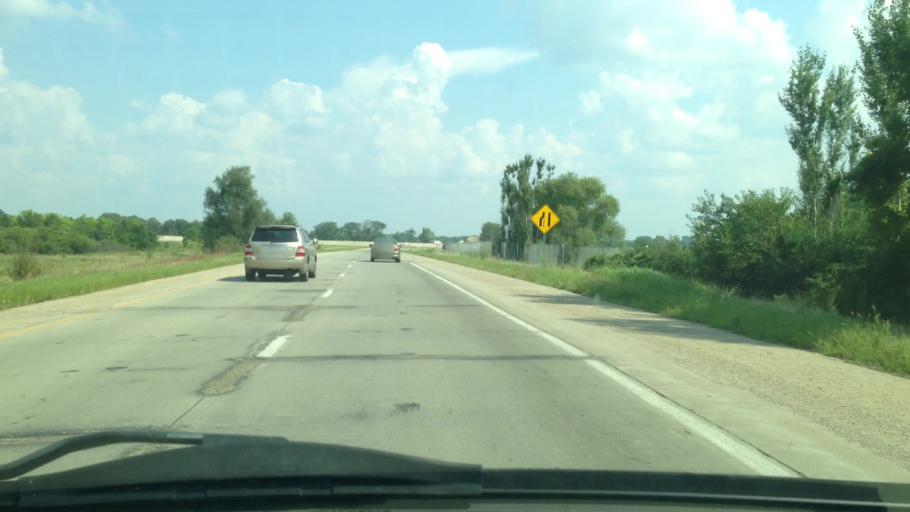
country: US
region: Iowa
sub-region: Black Hawk County
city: Cedar Falls
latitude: 42.5363
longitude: -92.3930
